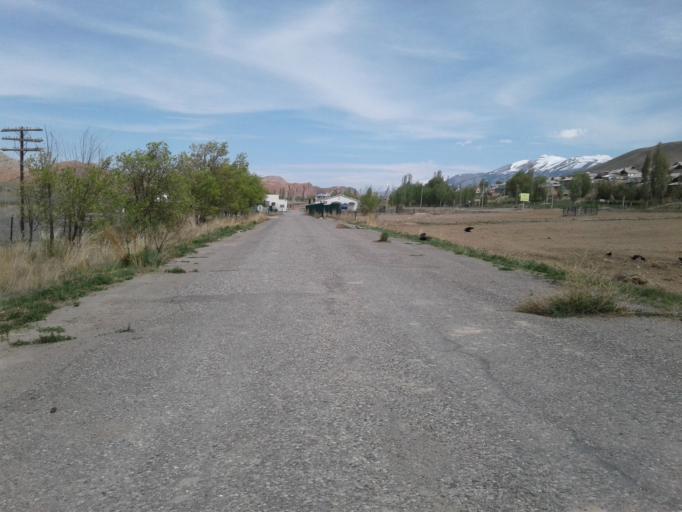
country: KG
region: Naryn
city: Naryn
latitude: 41.4306
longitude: 75.9032
